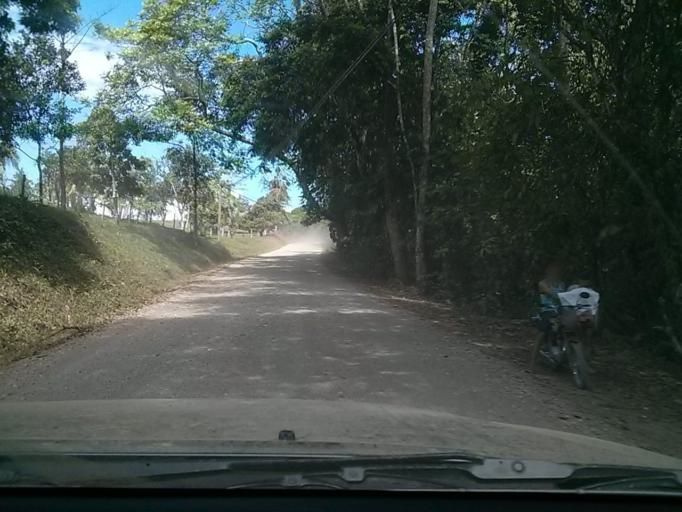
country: CR
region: Puntarenas
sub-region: Canton de Golfito
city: Golfito
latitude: 8.4496
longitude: -83.0570
